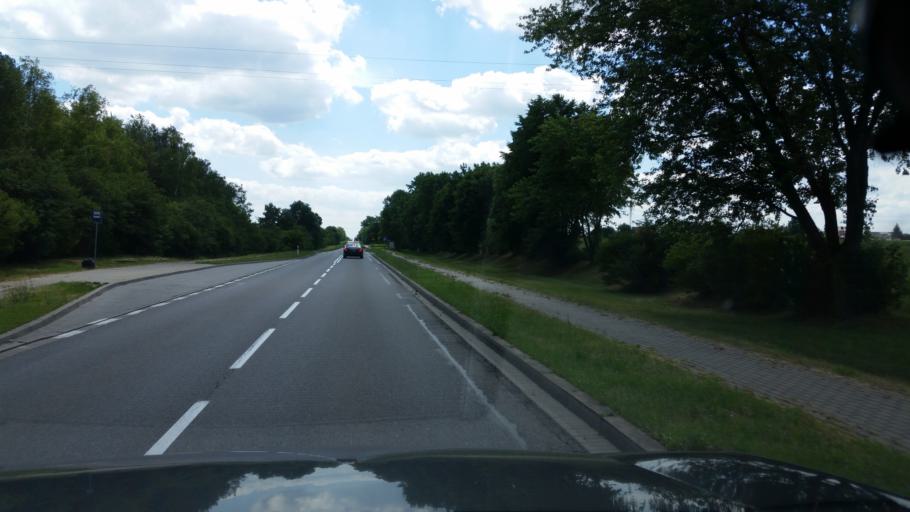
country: PL
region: Masovian Voivodeship
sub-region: Powiat ostrowski
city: Ostrow Mazowiecka
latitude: 52.8650
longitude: 21.8666
